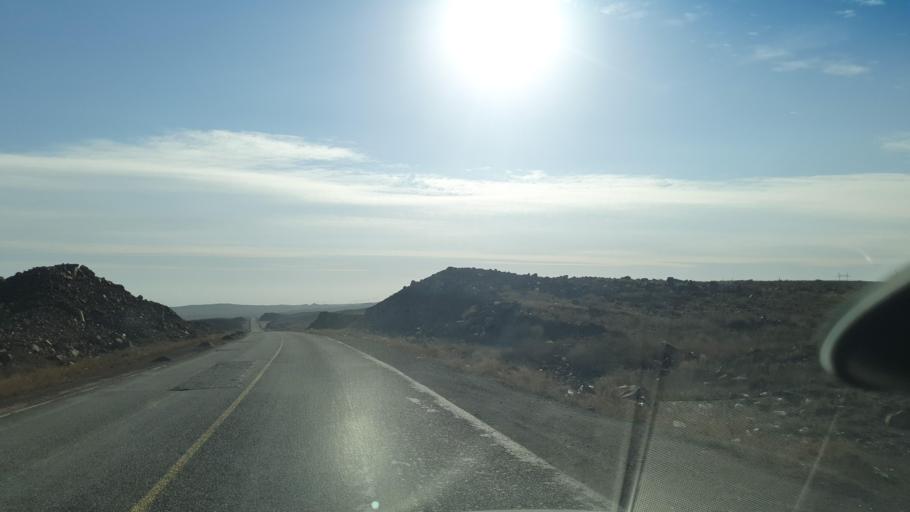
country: KZ
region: Zhambyl
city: Mynaral
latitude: 45.7042
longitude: 73.3974
